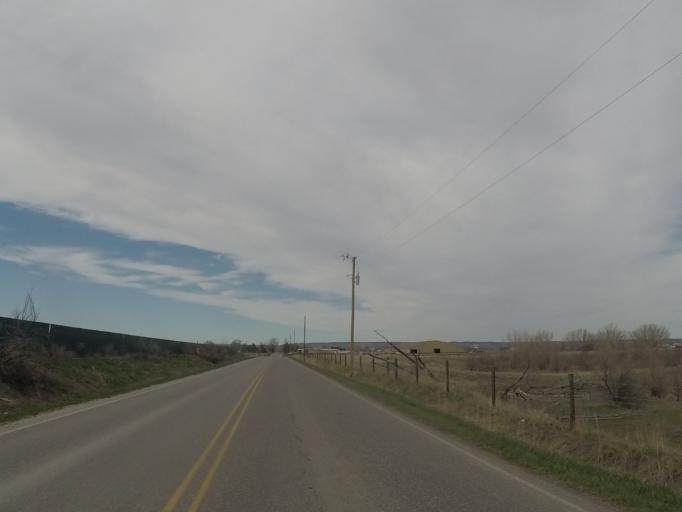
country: US
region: Montana
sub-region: Yellowstone County
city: Laurel
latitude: 45.7151
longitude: -108.6587
